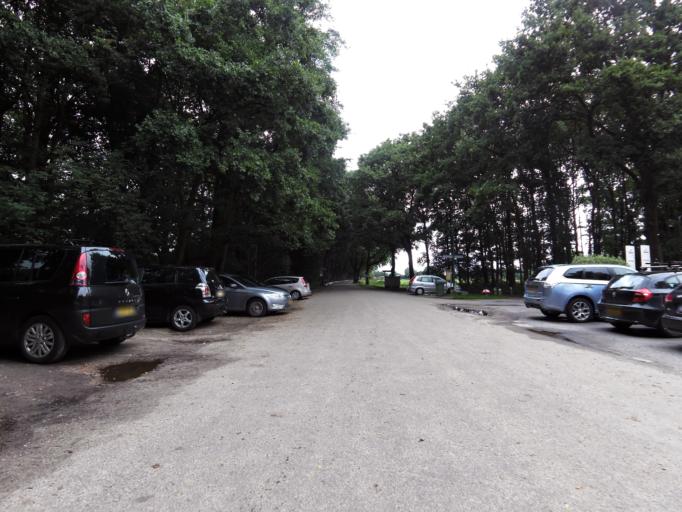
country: NL
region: North Brabant
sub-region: Gemeente Waalwijk
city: Waalwijk
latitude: 51.6563
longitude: 5.0822
